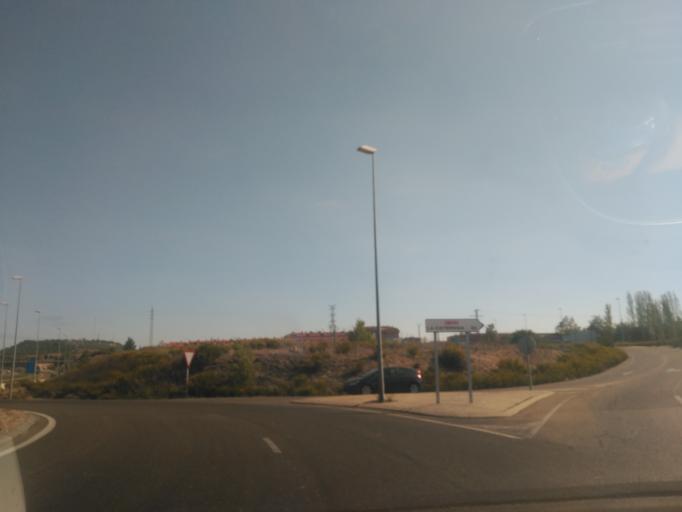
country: ES
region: Castille and Leon
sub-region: Provincia de Valladolid
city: Cisterniga
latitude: 41.6198
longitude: -4.6935
